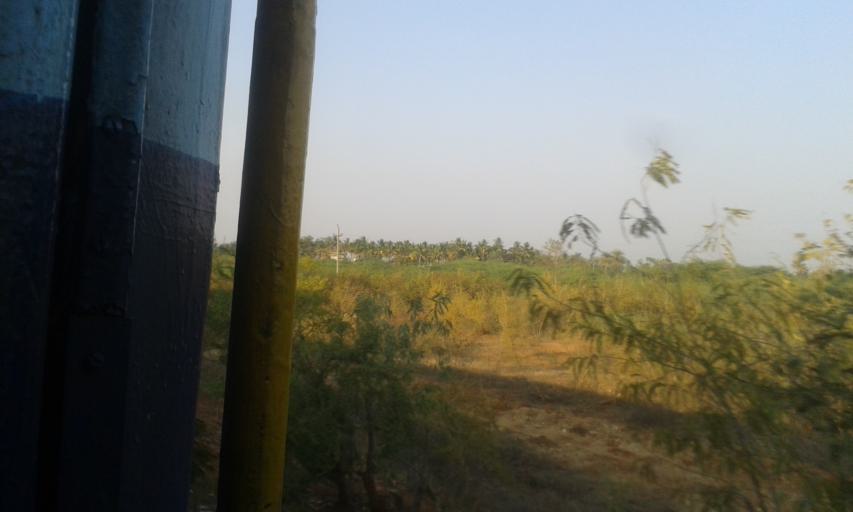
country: IN
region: Karnataka
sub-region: Chikkaballapur
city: Gauribidanur
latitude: 13.5794
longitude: 77.5055
